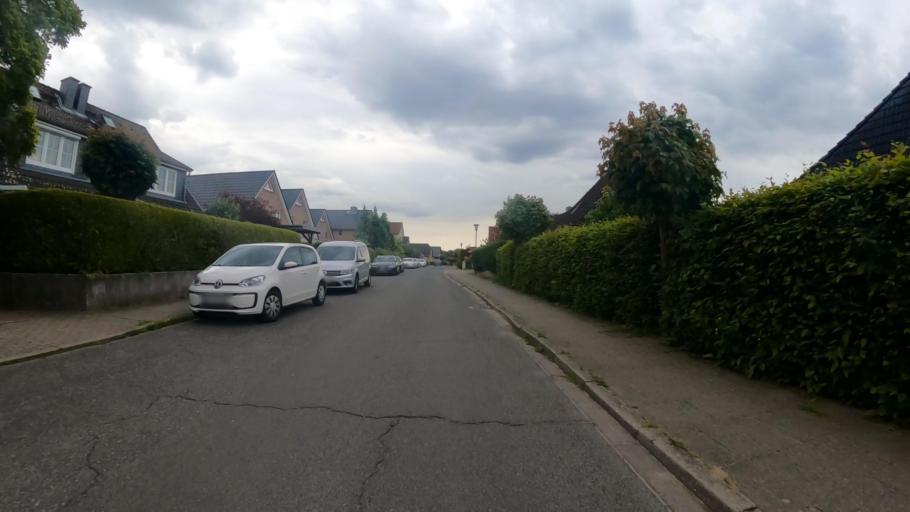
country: DE
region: Schleswig-Holstein
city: Rellingen
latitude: 53.6446
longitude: 9.8186
